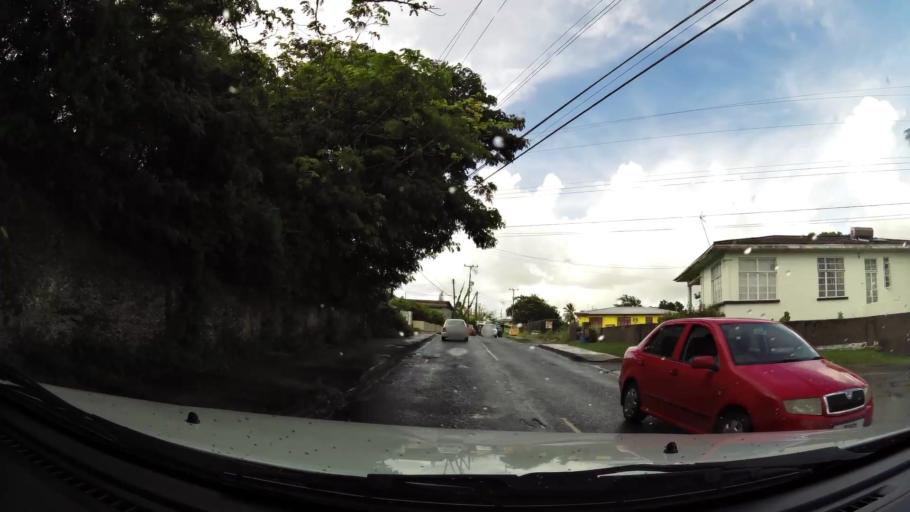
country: BB
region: Saint Michael
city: Bridgetown
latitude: 13.1364
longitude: -59.6065
